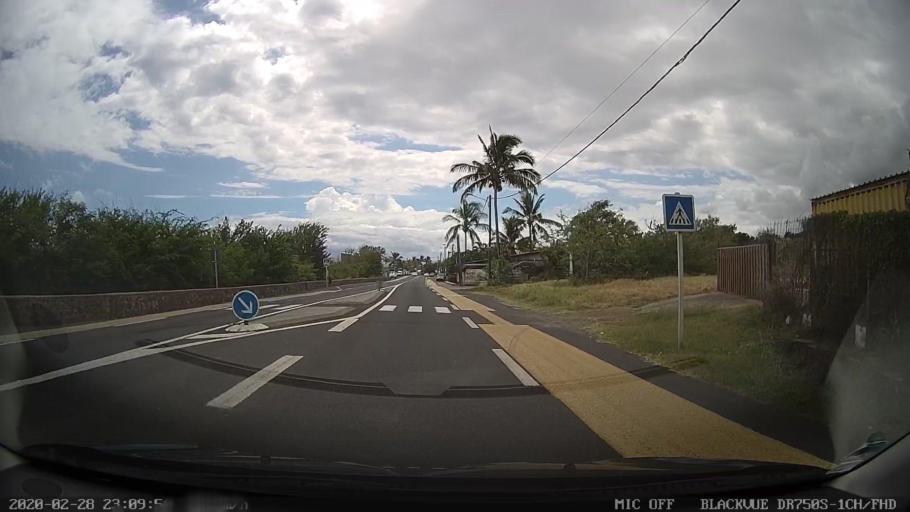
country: RE
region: Reunion
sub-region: Reunion
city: Trois-Bassins
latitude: -21.1228
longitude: 55.2634
